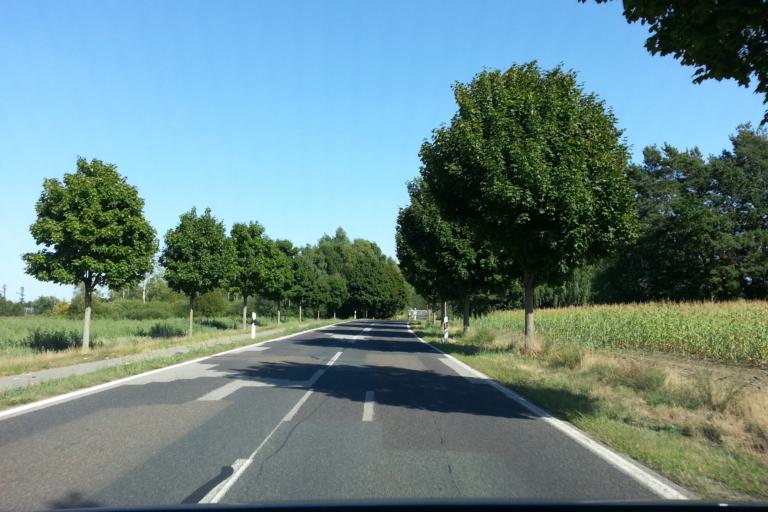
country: DE
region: Mecklenburg-Vorpommern
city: Eggesin
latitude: 53.6811
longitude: 14.0414
